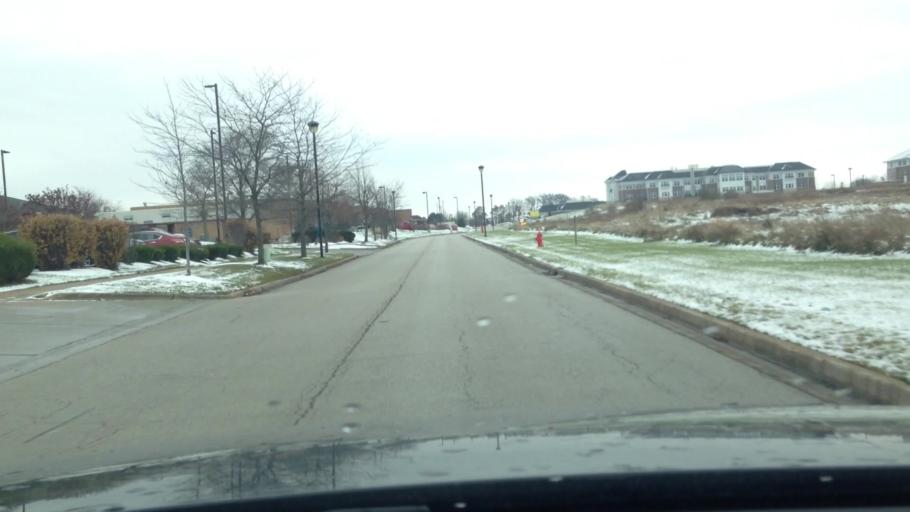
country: US
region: Illinois
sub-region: McHenry County
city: Huntley
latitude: 42.1532
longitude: -88.4344
